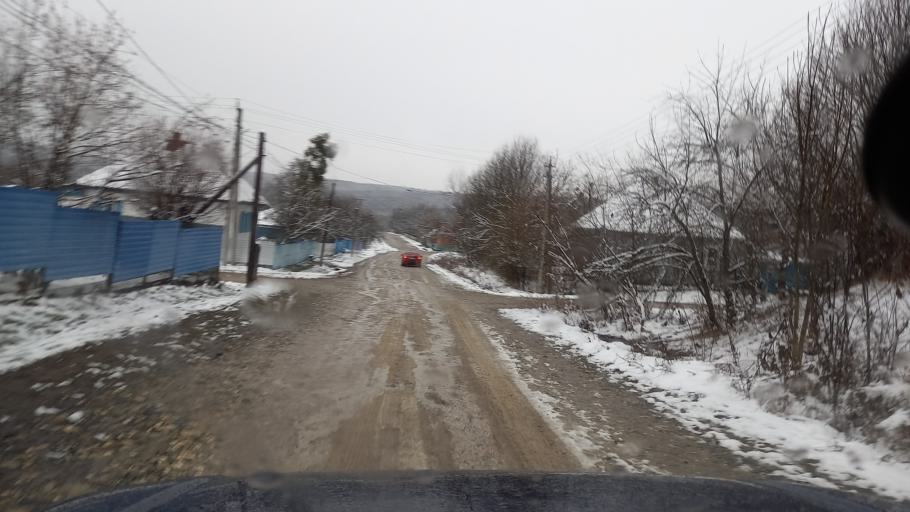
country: RU
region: Adygeya
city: Abadzekhskaya
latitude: 44.3514
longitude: 40.4122
